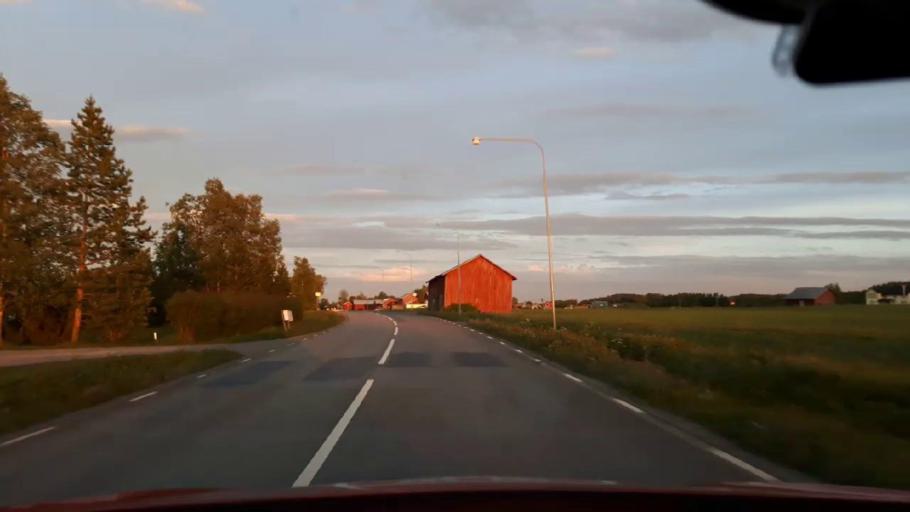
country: SE
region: Jaemtland
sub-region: OEstersunds Kommun
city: Brunflo
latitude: 63.1018
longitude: 14.7387
